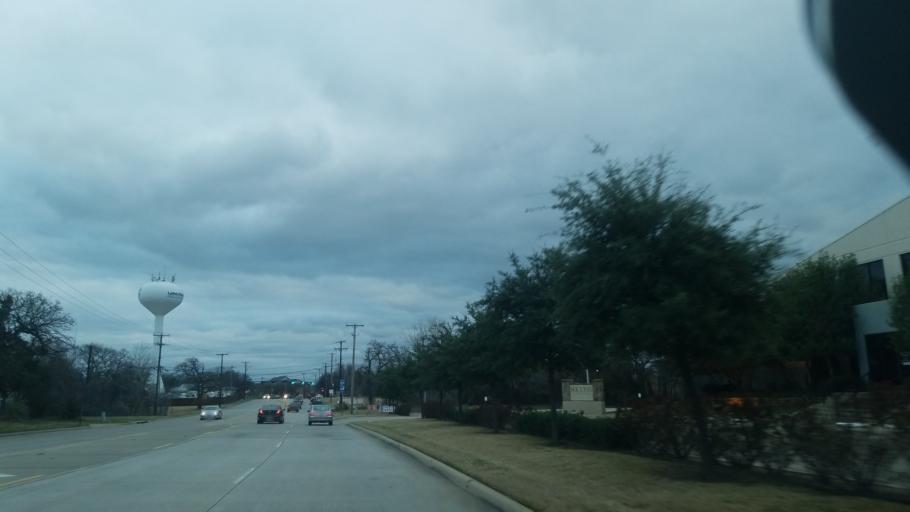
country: US
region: Texas
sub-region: Denton County
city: Hickory Creek
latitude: 33.1298
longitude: -97.0329
